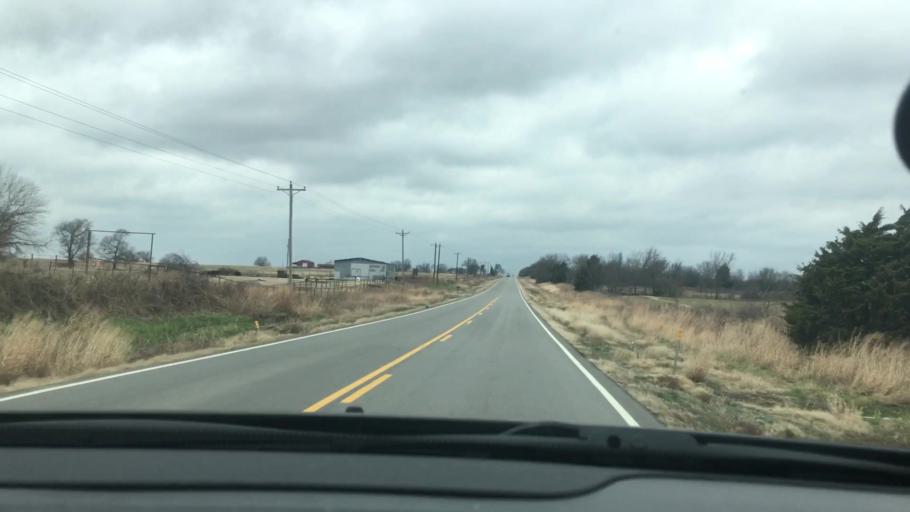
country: US
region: Oklahoma
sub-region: Atoka County
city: Atoka
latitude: 34.3749
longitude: -96.2396
